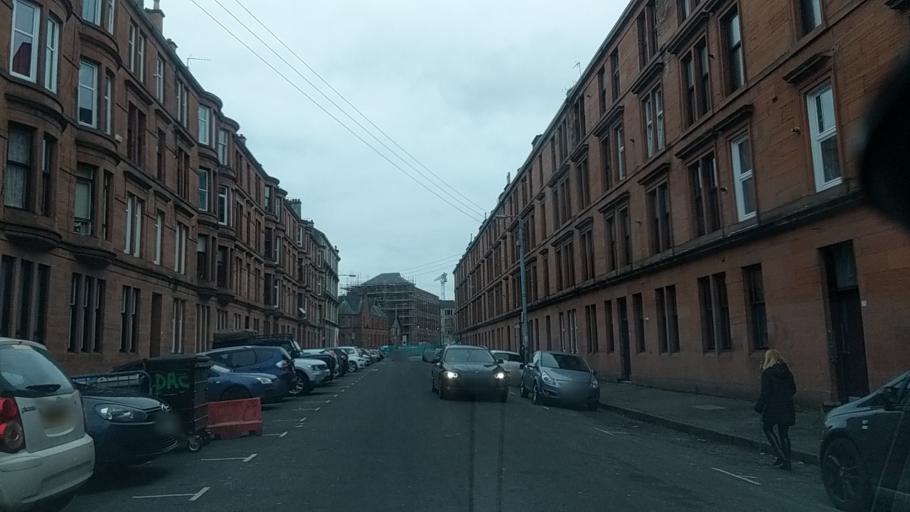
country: GB
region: Scotland
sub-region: Glasgow City
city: Glasgow
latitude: 55.8722
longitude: -4.3042
